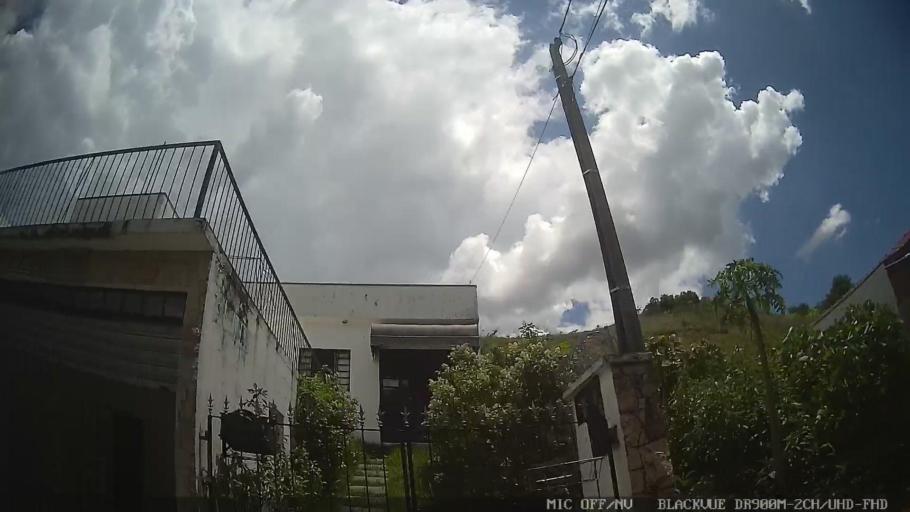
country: BR
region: Sao Paulo
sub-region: Serra Negra
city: Serra Negra
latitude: -22.5949
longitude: -46.7177
